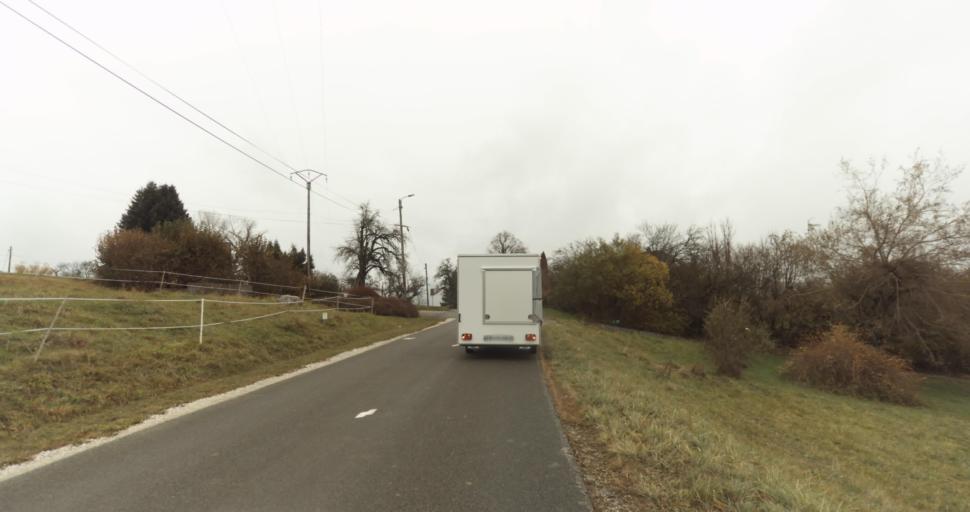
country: FR
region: Rhone-Alpes
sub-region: Departement de la Haute-Savoie
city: Groisy
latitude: 46.0245
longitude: 6.1830
